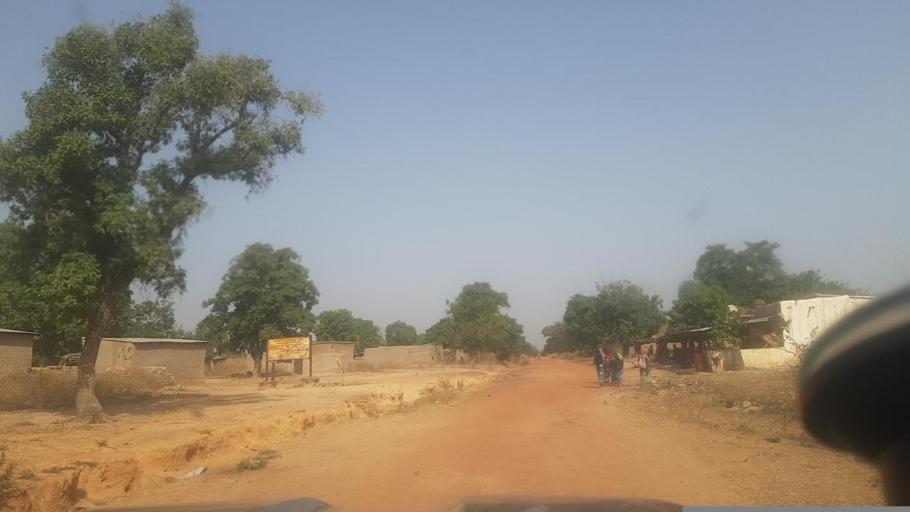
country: ML
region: Segou
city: Bla
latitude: 12.8494
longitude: -5.9891
